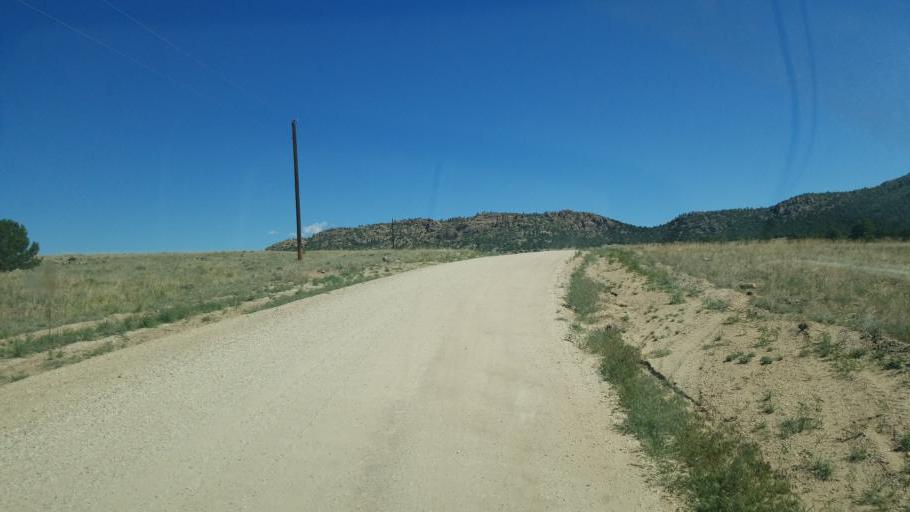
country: US
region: Colorado
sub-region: Custer County
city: Westcliffe
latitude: 38.2227
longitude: -105.4581
